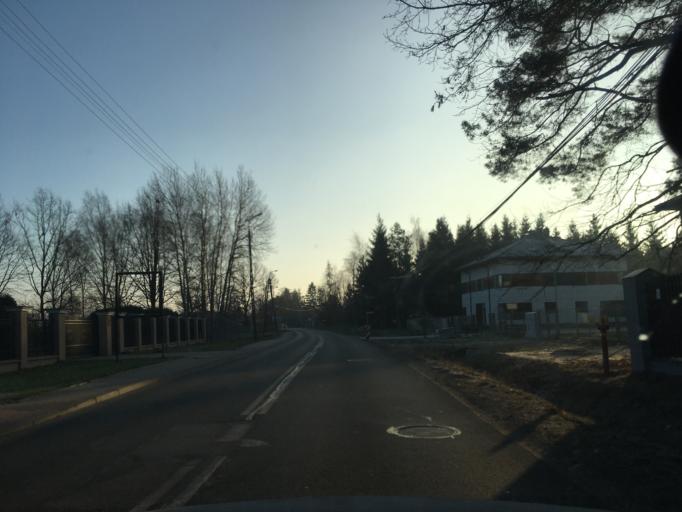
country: PL
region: Masovian Voivodeship
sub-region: Powiat piaseczynski
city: Piaseczno
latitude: 52.0701
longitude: 20.9830
